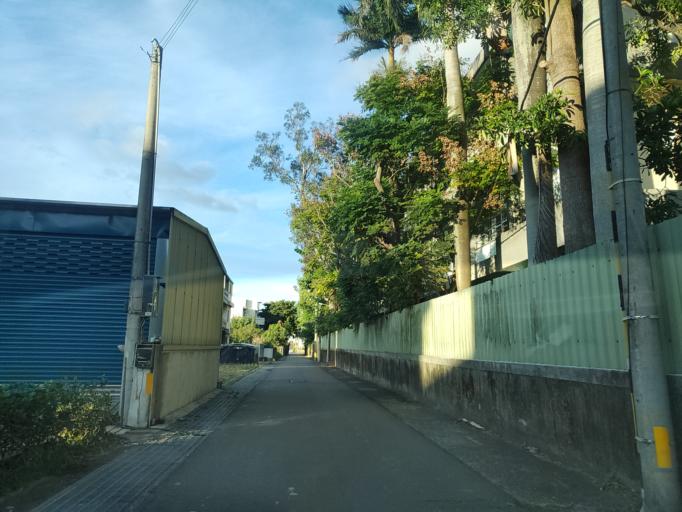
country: TW
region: Taiwan
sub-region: Miaoli
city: Miaoli
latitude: 24.5567
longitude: 120.8316
